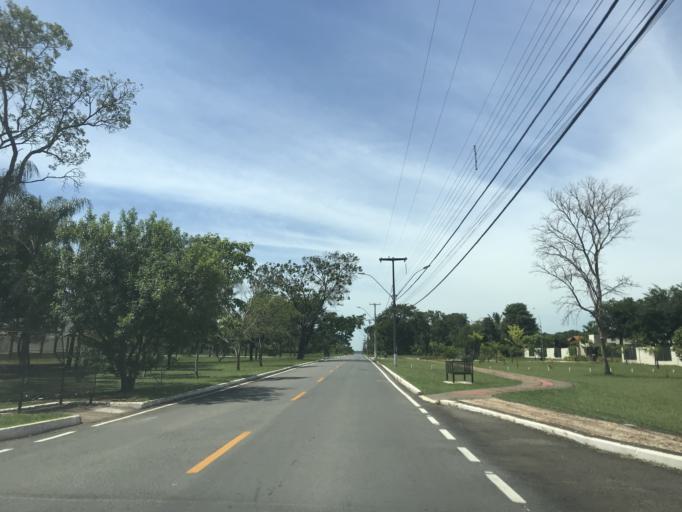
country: BR
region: Federal District
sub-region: Brasilia
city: Brasilia
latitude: -15.9008
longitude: -47.9329
